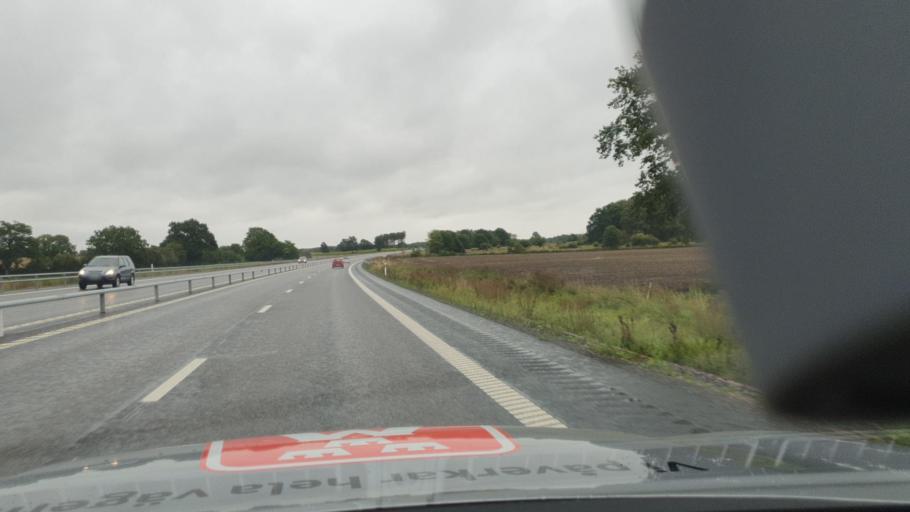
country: SE
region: Skane
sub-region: Kristianstads Kommun
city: Onnestad
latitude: 55.9709
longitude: 14.0429
